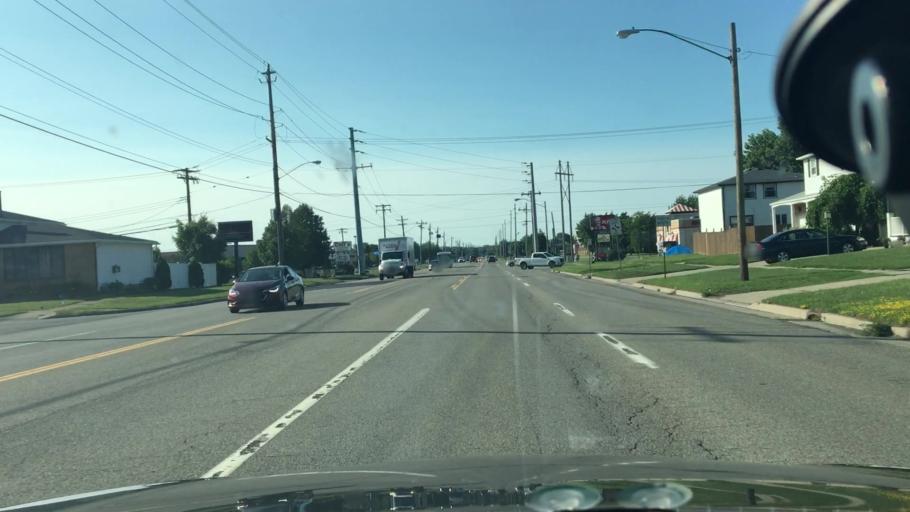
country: US
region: New York
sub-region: Erie County
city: Cheektowaga
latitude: 42.9157
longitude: -78.7351
